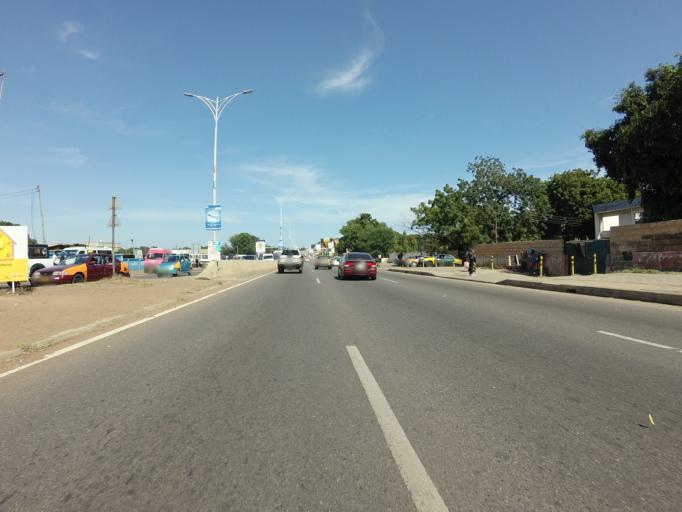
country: GH
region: Greater Accra
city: Accra
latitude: 5.5888
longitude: -0.1809
